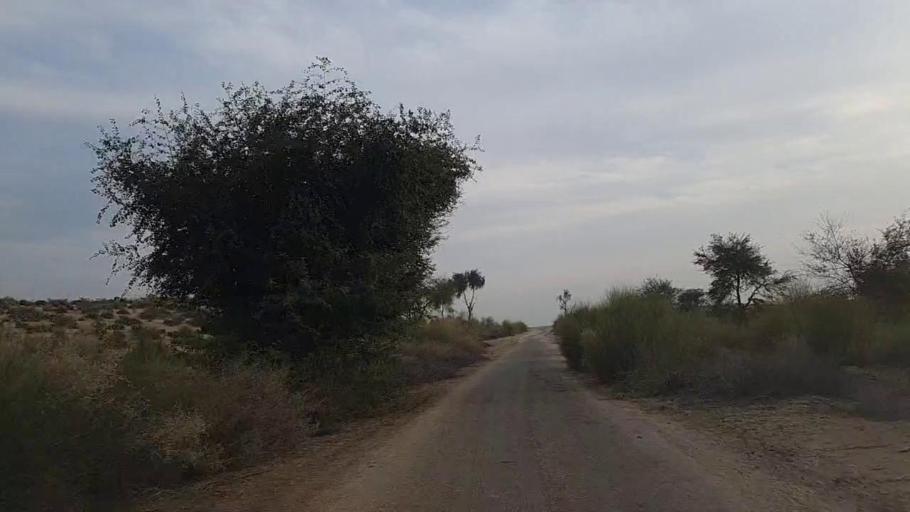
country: PK
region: Sindh
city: Jam Sahib
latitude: 26.4854
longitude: 68.5602
